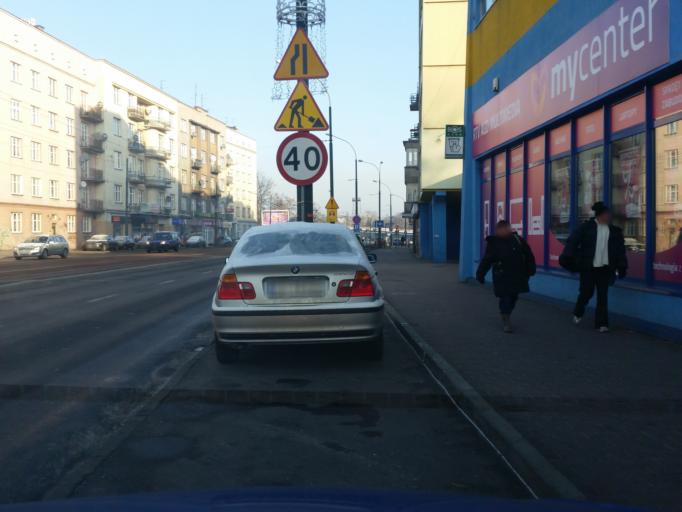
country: PL
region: Silesian Voivodeship
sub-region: Sosnowiec
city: Sosnowiec
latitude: 50.2798
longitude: 19.1307
